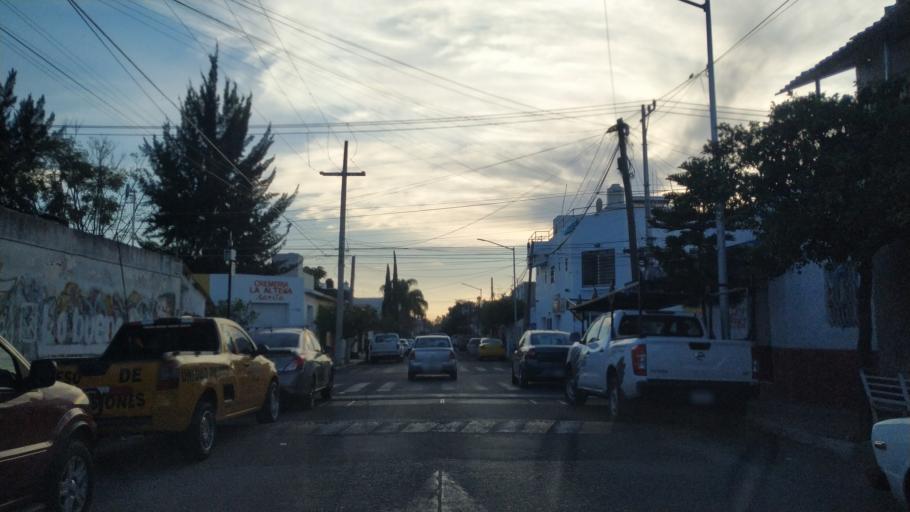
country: MX
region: Jalisco
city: Tlaquepaque
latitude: 20.6499
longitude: -103.3288
